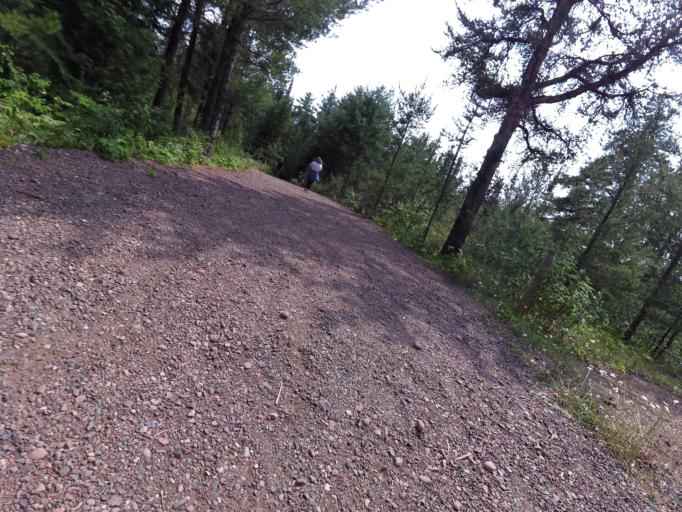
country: CA
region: Ontario
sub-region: Thunder Bay District
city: Thunder Bay
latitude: 48.8016
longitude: -88.6164
